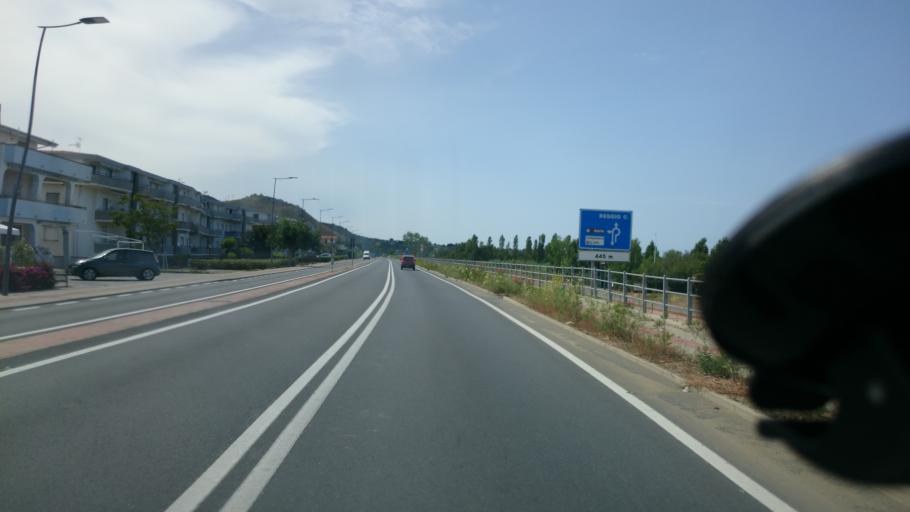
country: IT
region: Calabria
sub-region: Provincia di Cosenza
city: Santa Maria del Cedro
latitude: 39.7353
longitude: 15.8091
